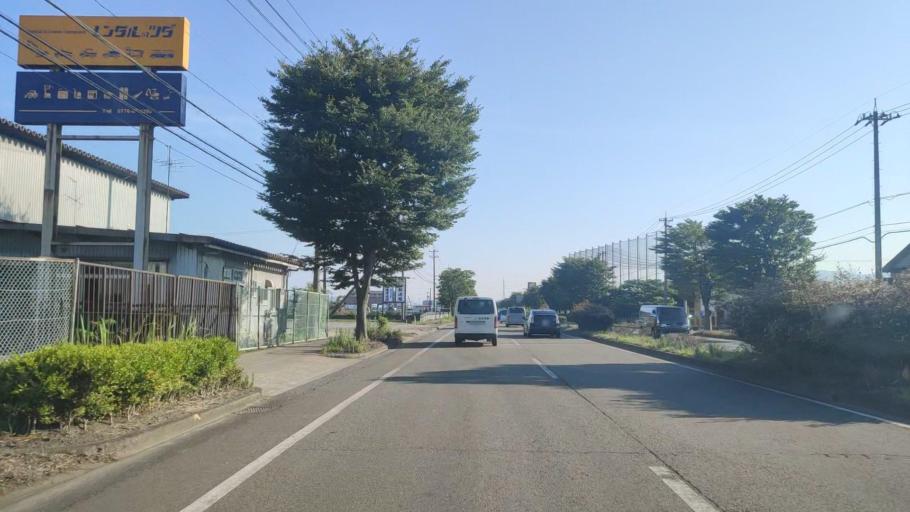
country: JP
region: Fukui
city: Maruoka
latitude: 36.1281
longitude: 136.2606
